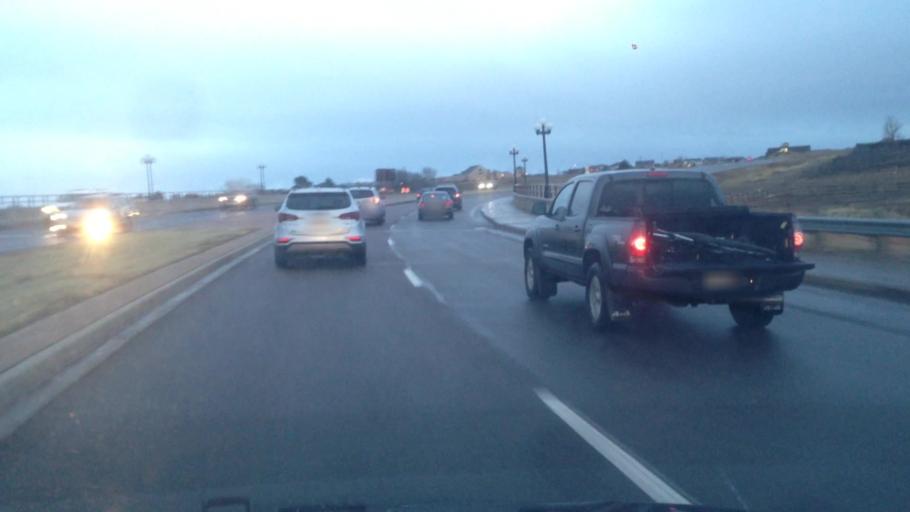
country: US
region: Colorado
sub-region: Douglas County
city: Stonegate
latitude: 39.5170
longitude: -104.8121
